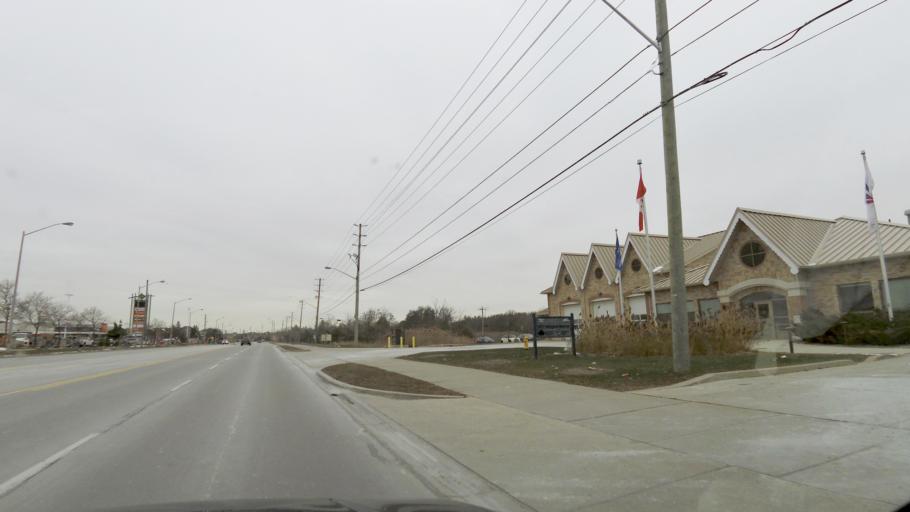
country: CA
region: Ontario
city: Vaughan
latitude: 43.8239
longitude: -79.6079
